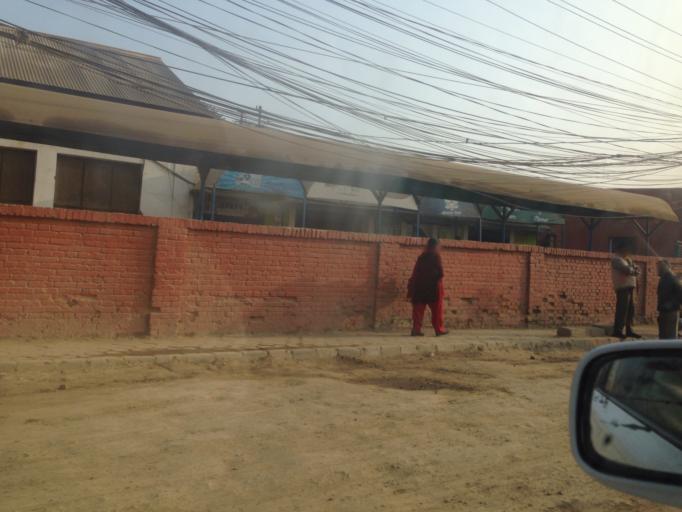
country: NP
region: Central Region
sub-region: Bagmati Zone
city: Kathmandu
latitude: 27.7173
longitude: 85.3151
